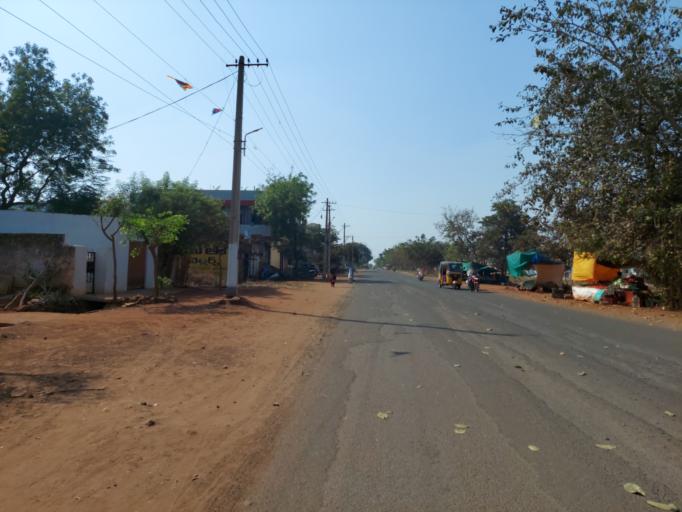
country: IN
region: Telangana
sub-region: Rangareddi
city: Vikarabad
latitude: 17.3390
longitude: 77.8973
